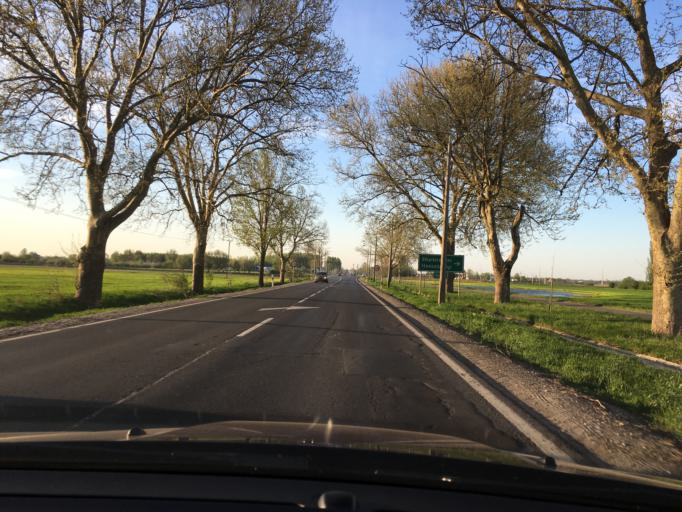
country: HU
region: Hajdu-Bihar
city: Mikepercs
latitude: 47.4812
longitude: 21.6337
